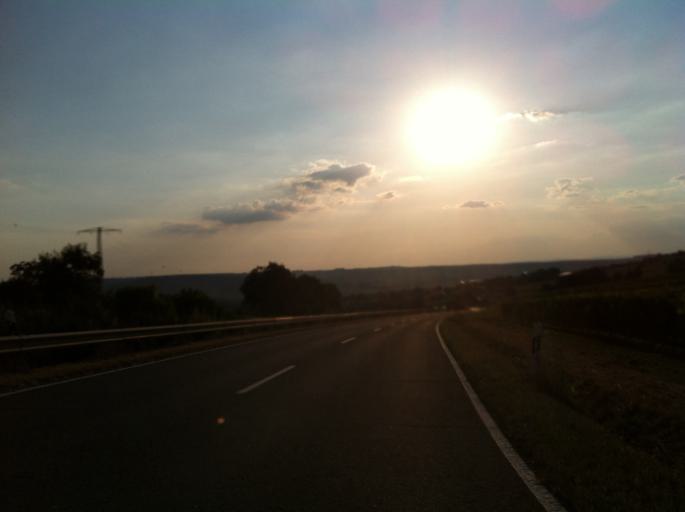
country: DE
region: Rheinland-Pfalz
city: Essenheim
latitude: 49.9237
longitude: 8.1391
